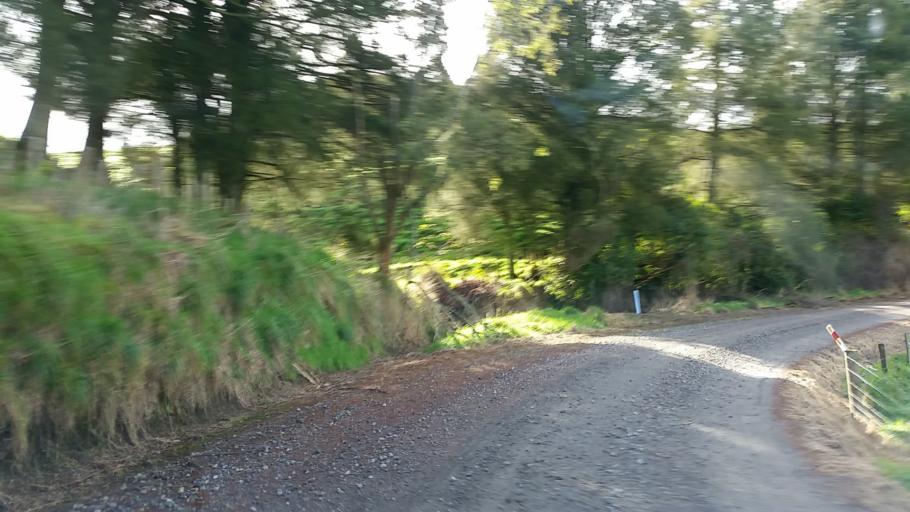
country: NZ
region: Taranaki
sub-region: South Taranaki District
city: Eltham
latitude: -39.2551
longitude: 174.5192
